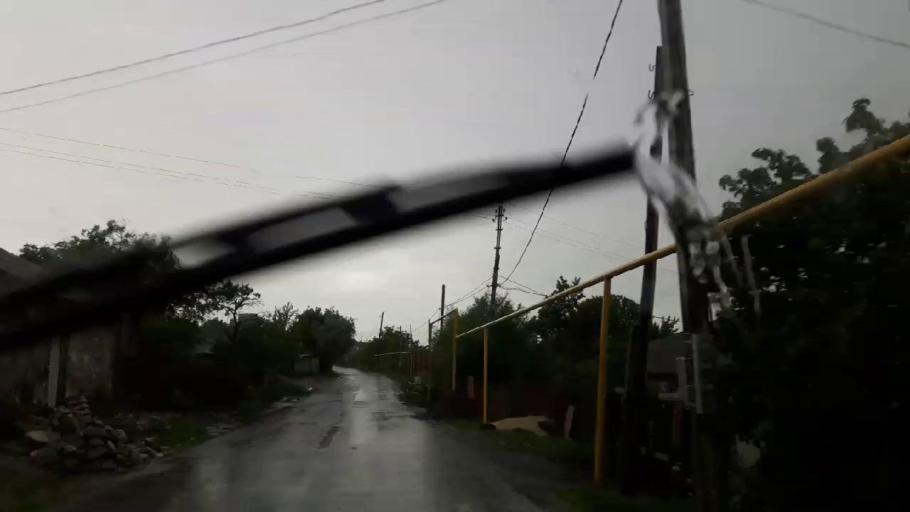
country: GE
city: Agara
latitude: 42.0175
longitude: 43.8378
